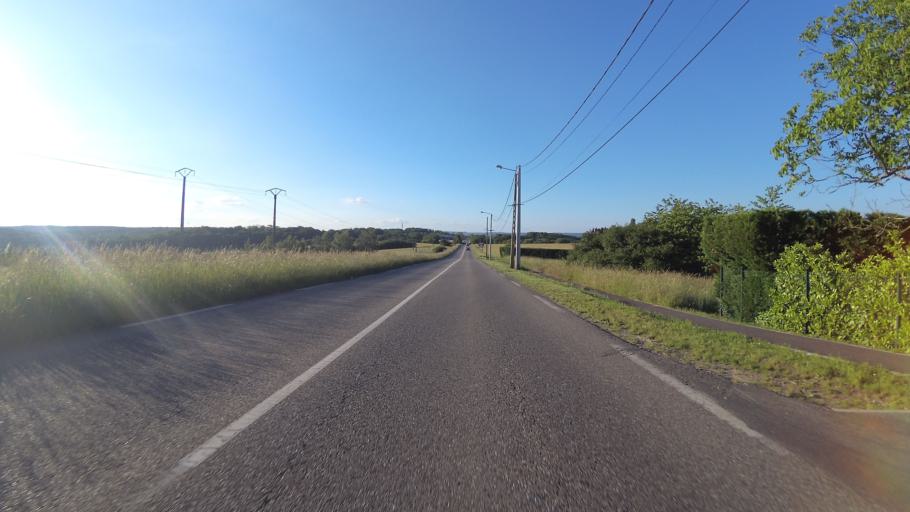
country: FR
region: Lorraine
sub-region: Departement de la Moselle
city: Remelfing
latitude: 49.0797
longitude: 7.0816
